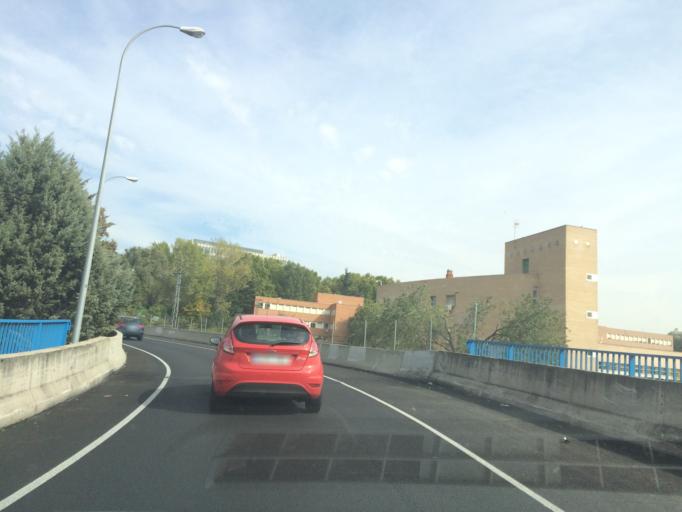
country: ES
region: Madrid
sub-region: Provincia de Madrid
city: Moncloa-Aravaca
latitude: 40.4500
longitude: -3.7418
